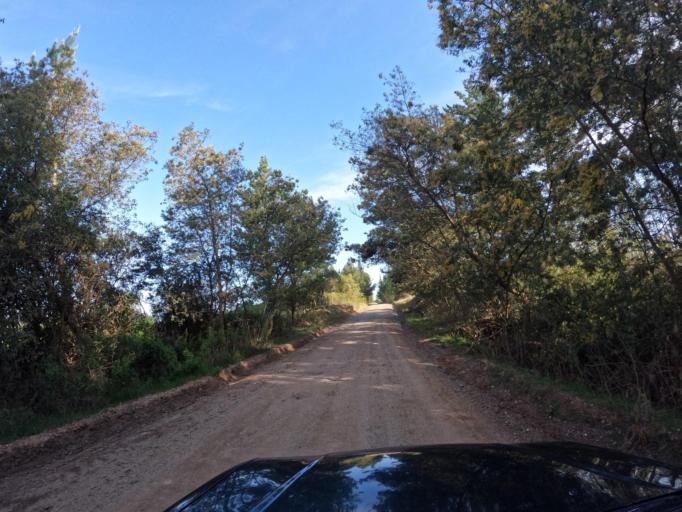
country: CL
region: Biobio
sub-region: Provincia de Biobio
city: La Laja
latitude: -37.1606
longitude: -72.7307
